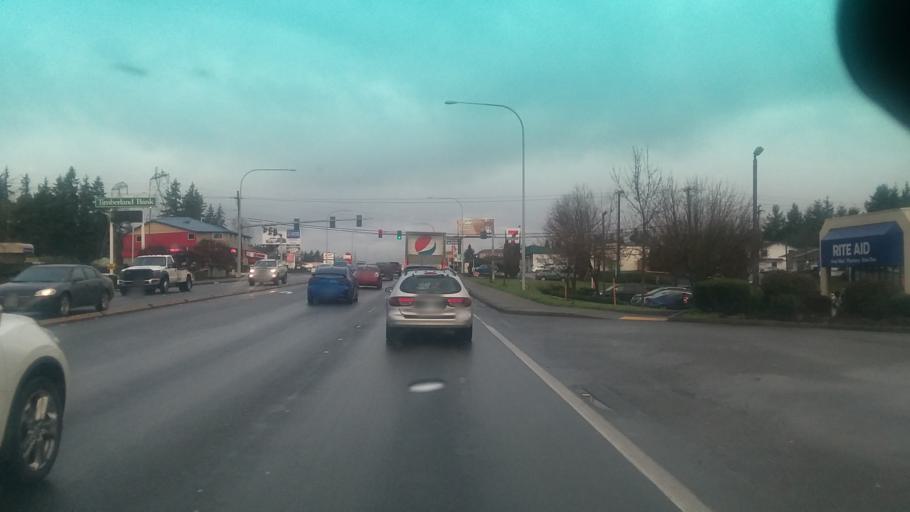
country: US
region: Washington
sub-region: Pierce County
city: South Hill
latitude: 47.1393
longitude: -122.2929
